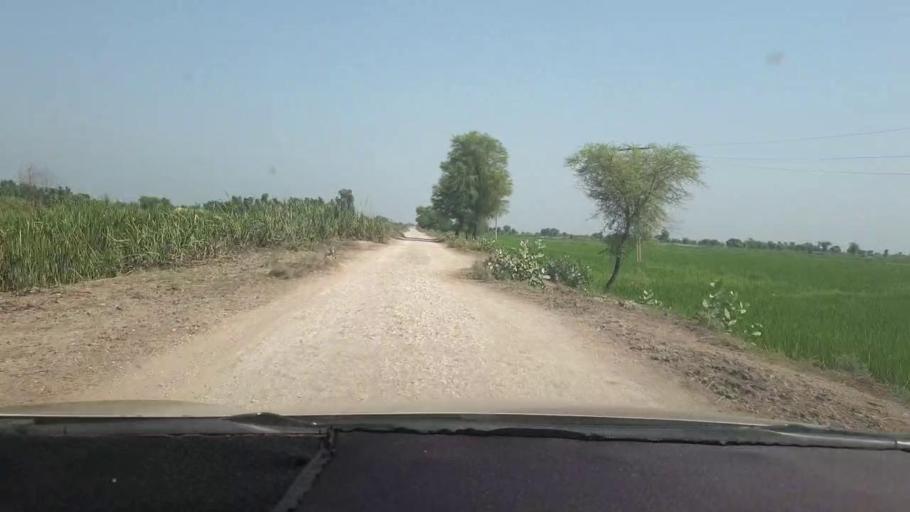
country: PK
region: Sindh
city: Miro Khan
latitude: 27.6738
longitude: 68.1372
